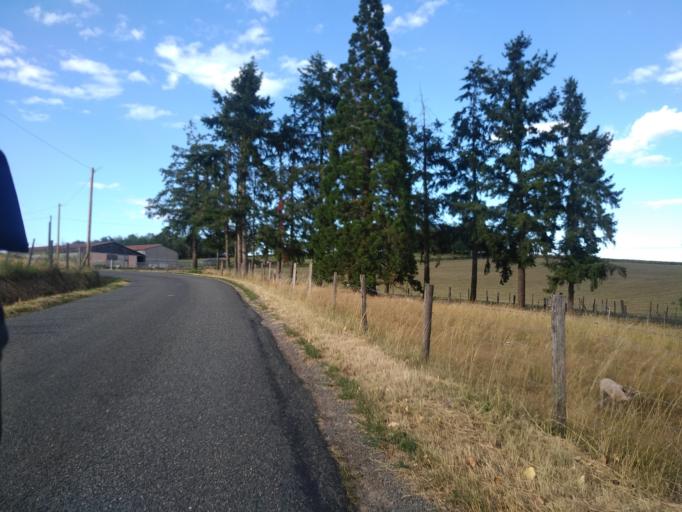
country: FR
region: Rhone-Alpes
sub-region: Departement de la Loire
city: Panissieres
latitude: 45.7464
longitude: 4.3493
